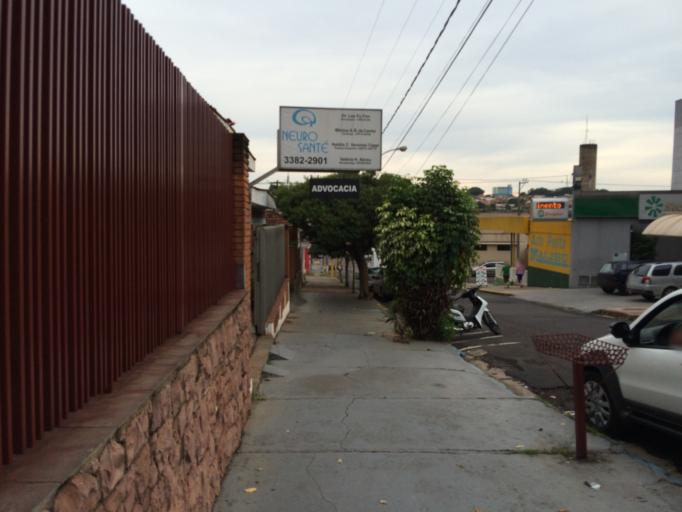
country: BR
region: Sao Paulo
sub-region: Matao
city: Matao
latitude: -21.6022
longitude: -48.3637
